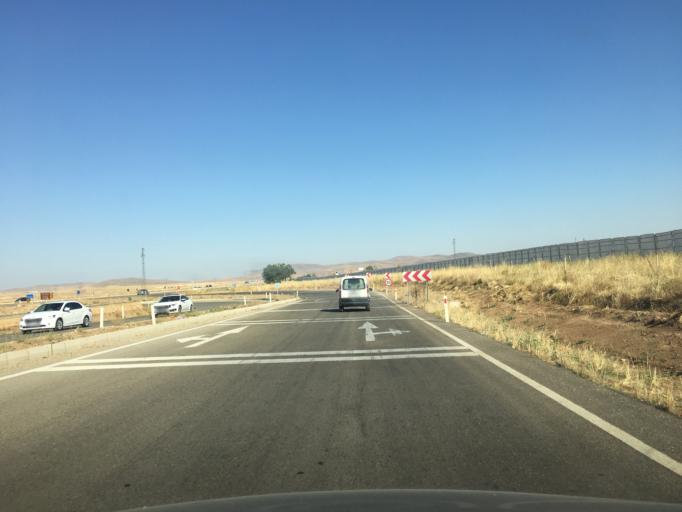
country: TR
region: Kirsehir
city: Akpinar
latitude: 39.3279
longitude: 34.0376
